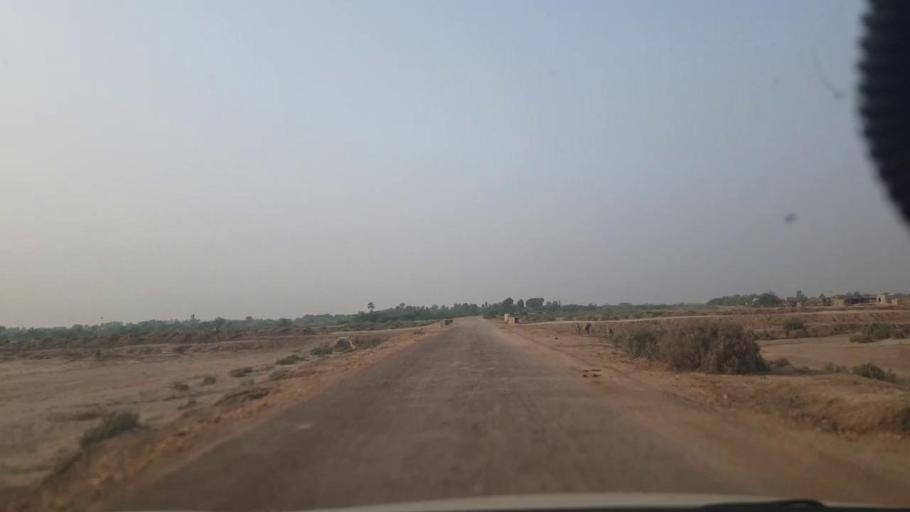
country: PK
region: Sindh
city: Bulri
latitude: 24.8204
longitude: 68.4042
